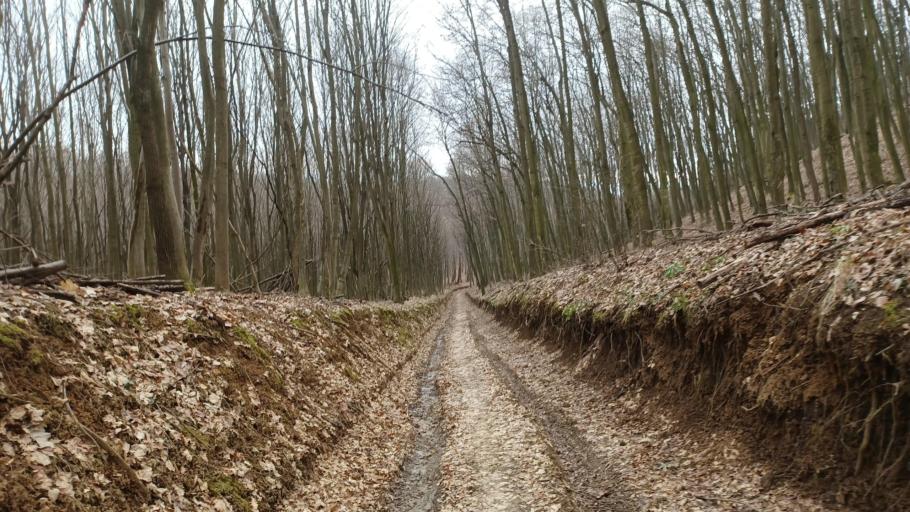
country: HU
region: Tolna
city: Szentgalpuszta
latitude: 46.3256
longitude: 18.6478
